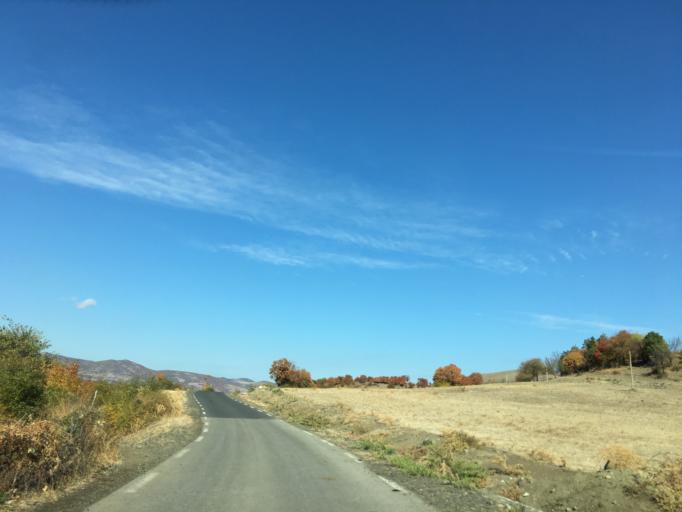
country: BG
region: Kurdzhali
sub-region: Obshtina Krumovgrad
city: Krumovgrad
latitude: 41.5019
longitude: 25.5233
